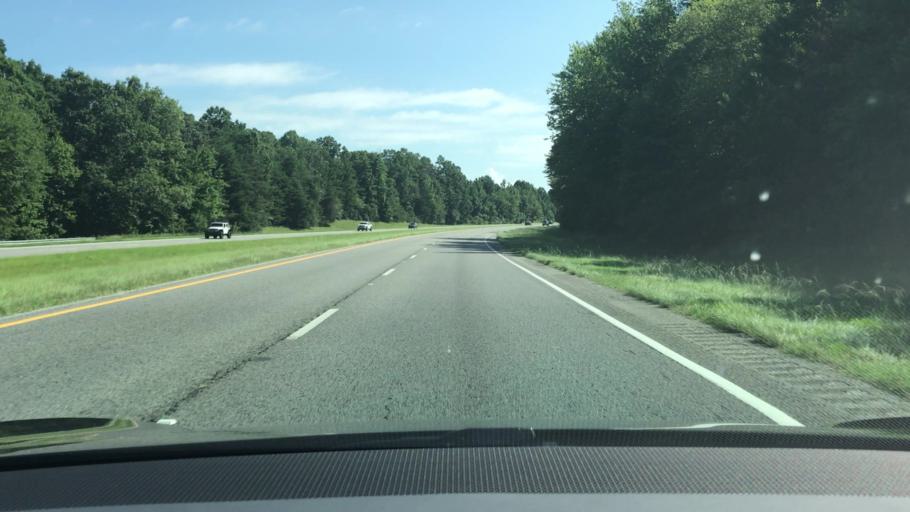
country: US
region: Georgia
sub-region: Habersham County
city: Baldwin
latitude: 34.5068
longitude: -83.5674
